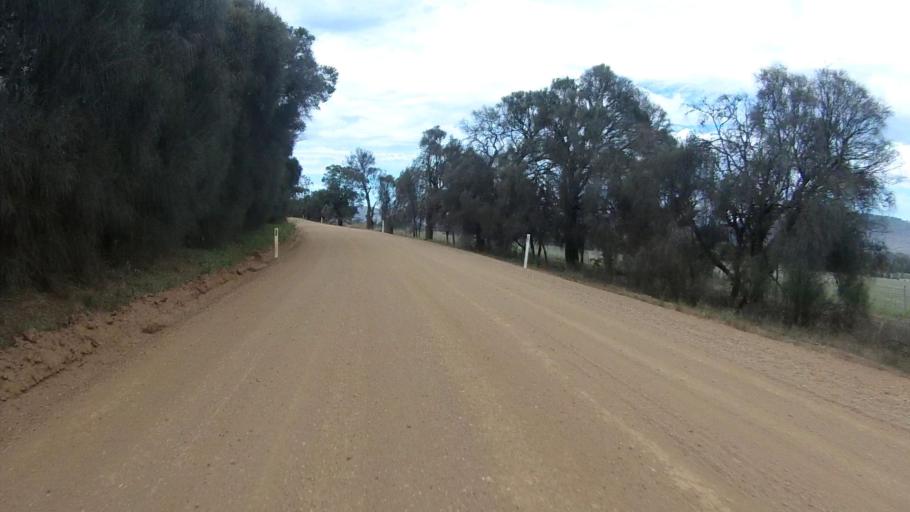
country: AU
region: Tasmania
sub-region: Sorell
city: Sorell
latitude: -42.7005
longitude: 147.4585
